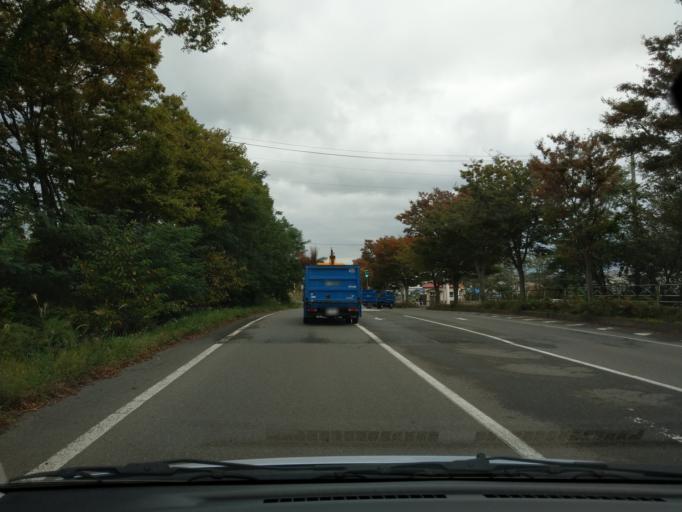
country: JP
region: Akita
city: Akita Shi
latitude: 39.6762
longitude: 140.0785
